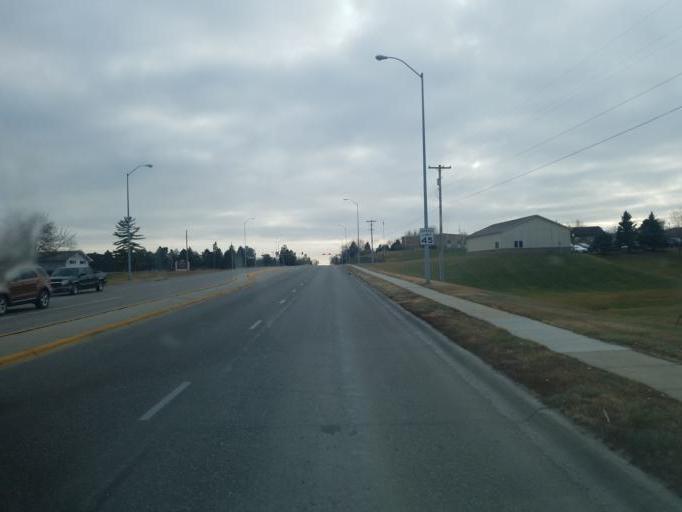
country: US
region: Nebraska
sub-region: Madison County
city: Norfolk
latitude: 42.0464
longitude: -97.4268
